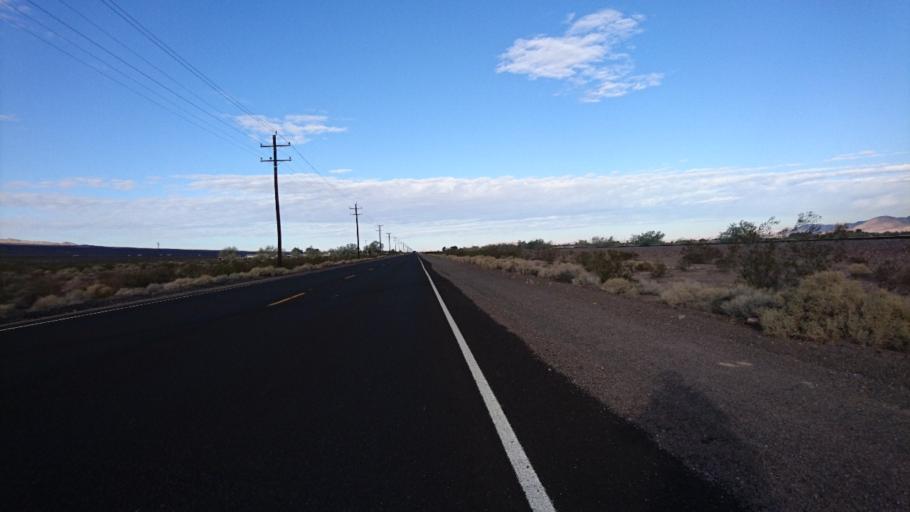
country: US
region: California
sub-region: San Bernardino County
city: Barstow
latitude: 34.8406
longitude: -116.7430
